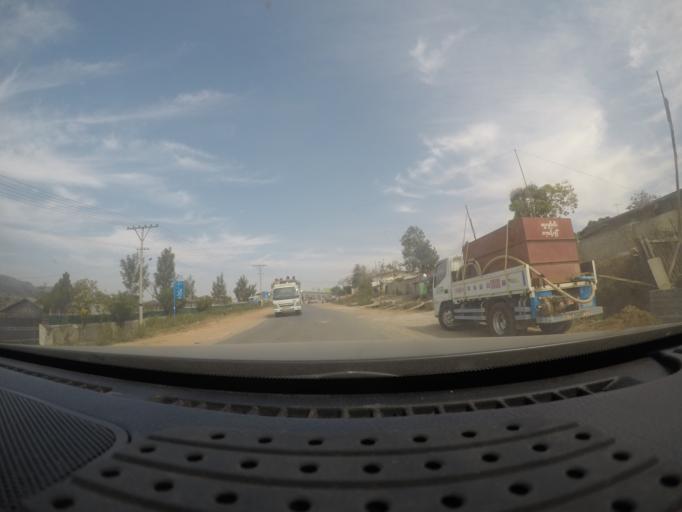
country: MM
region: Shan
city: Taunggyi
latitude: 20.6663
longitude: 96.6283
